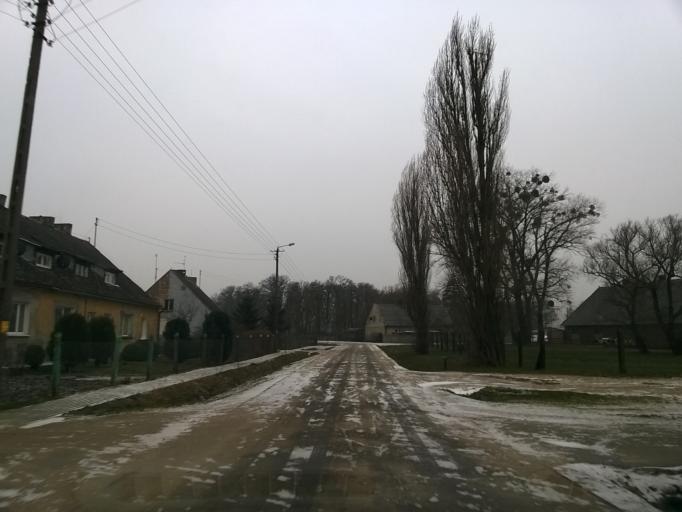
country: PL
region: Kujawsko-Pomorskie
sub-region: Powiat nakielski
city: Kcynia
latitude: 53.0103
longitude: 17.5016
